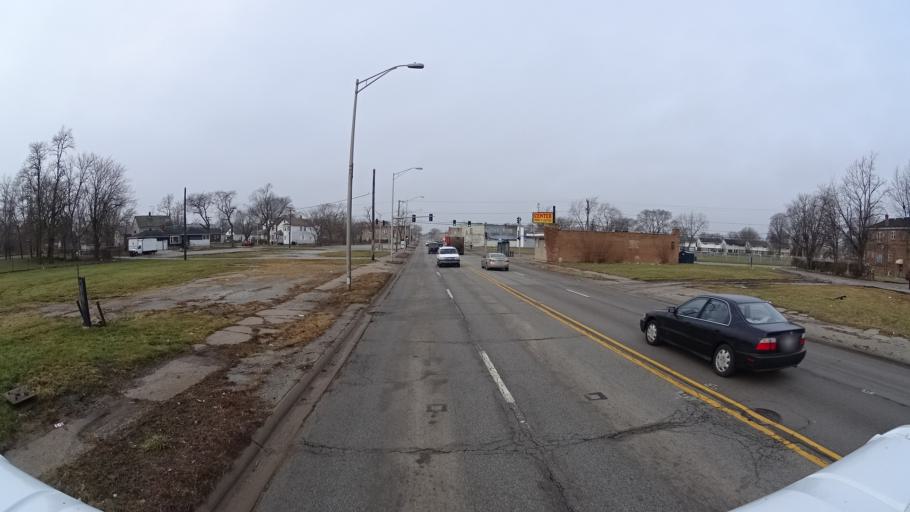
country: US
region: Illinois
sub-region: Cook County
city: Chicago Heights
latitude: 41.5062
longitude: -87.6266
